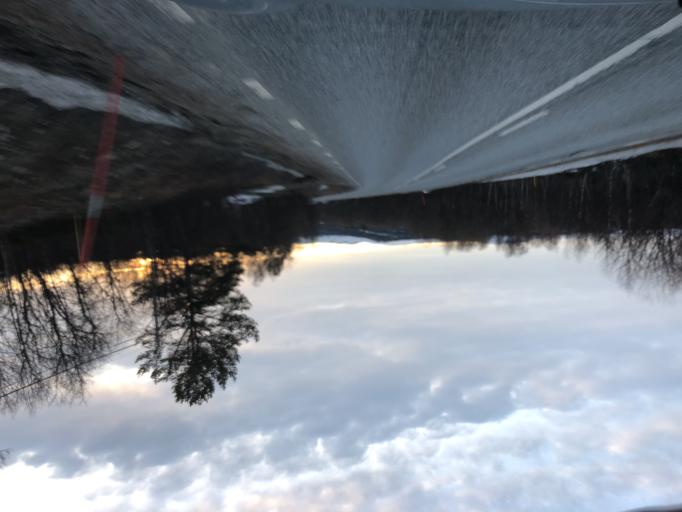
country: NO
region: Hedmark
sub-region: Engerdal
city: Engerdal
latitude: 62.5348
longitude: 12.3665
